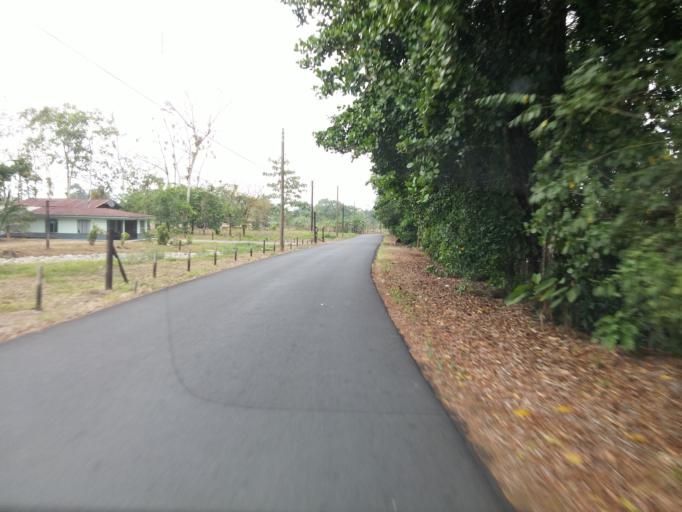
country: CR
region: Alajuela
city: Quesada
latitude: 10.3365
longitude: -84.5155
